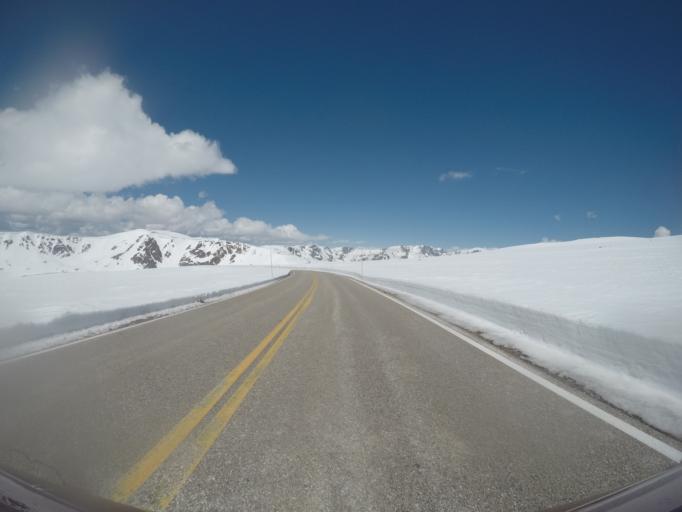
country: US
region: Montana
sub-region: Carbon County
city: Red Lodge
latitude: 44.9712
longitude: -109.4412
